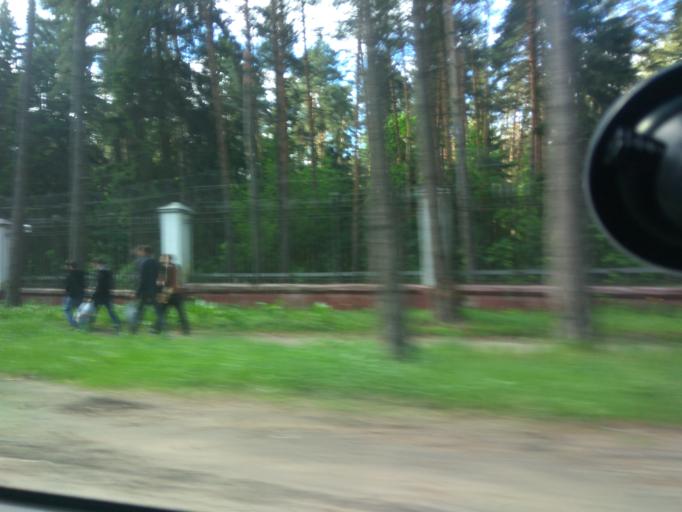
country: RU
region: Moskovskaya
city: Kratovo
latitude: 55.5770
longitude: 38.1610
